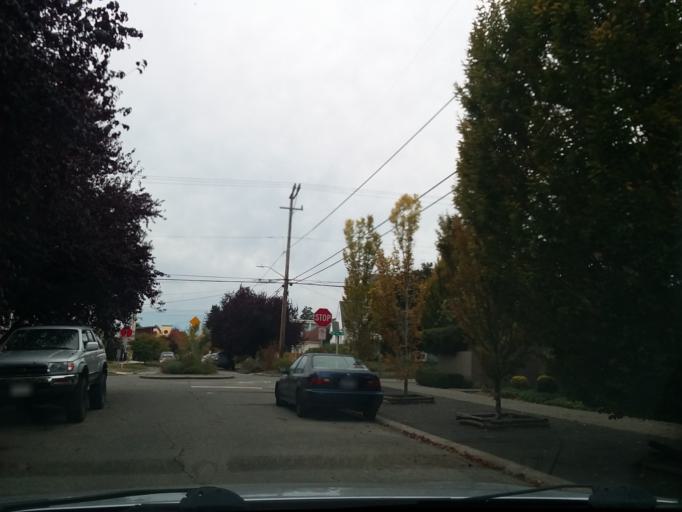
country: US
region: Washington
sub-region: King County
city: Seattle
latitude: 47.6731
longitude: -122.3785
